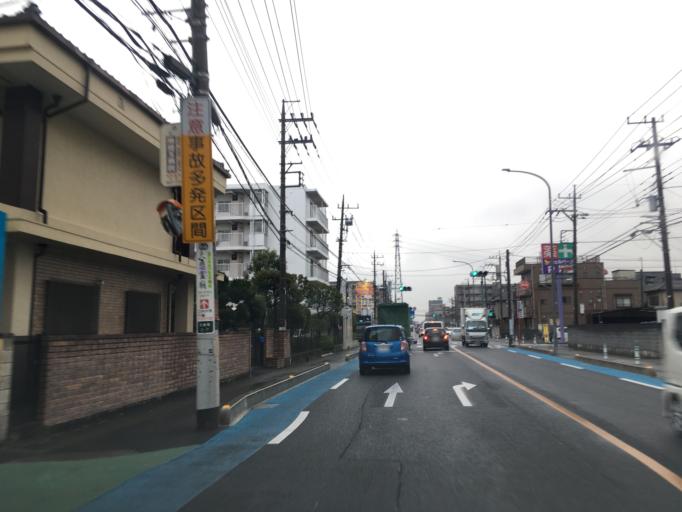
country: JP
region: Saitama
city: Koshigaya
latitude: 35.8840
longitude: 139.7923
